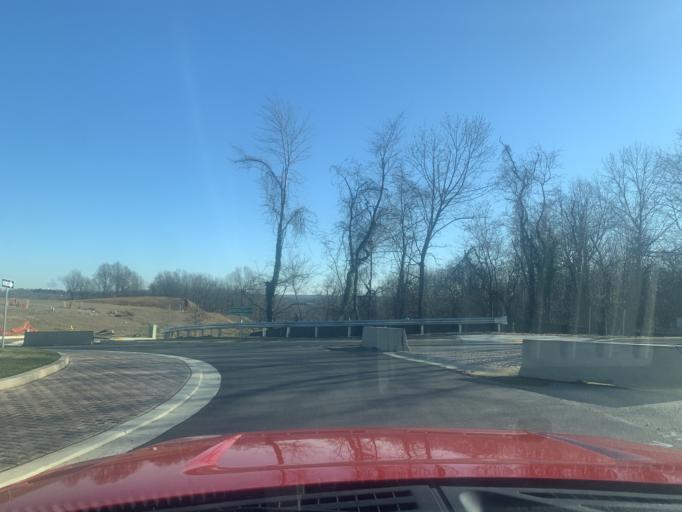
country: US
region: Maryland
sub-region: Anne Arundel County
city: Brooklyn Park
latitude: 39.2109
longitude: -76.6118
